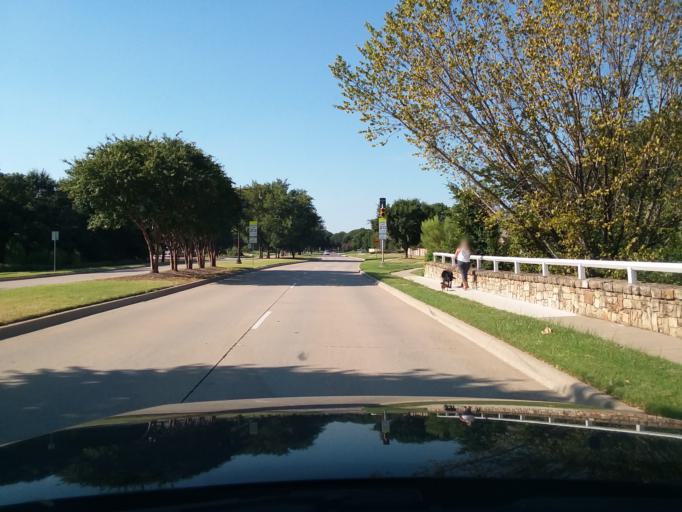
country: US
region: Texas
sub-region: Denton County
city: Double Oak
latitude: 33.0509
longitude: -97.0933
